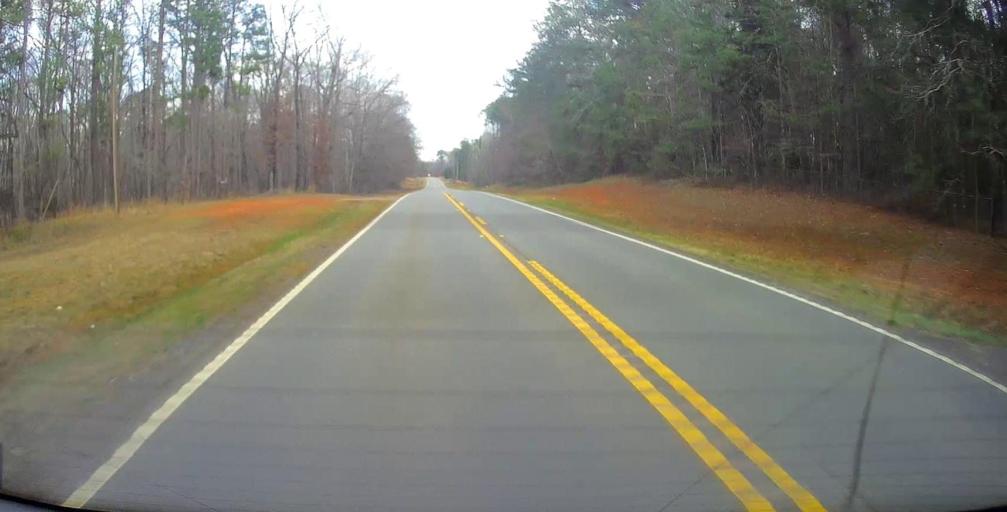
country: US
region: Georgia
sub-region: Harris County
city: Hamilton
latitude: 32.7018
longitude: -84.8416
